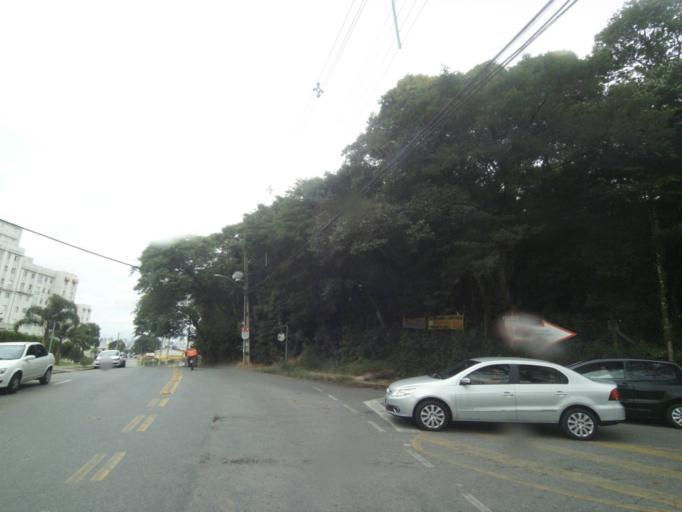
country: BR
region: Parana
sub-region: Curitiba
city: Curitiba
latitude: -25.4625
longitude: -49.3290
